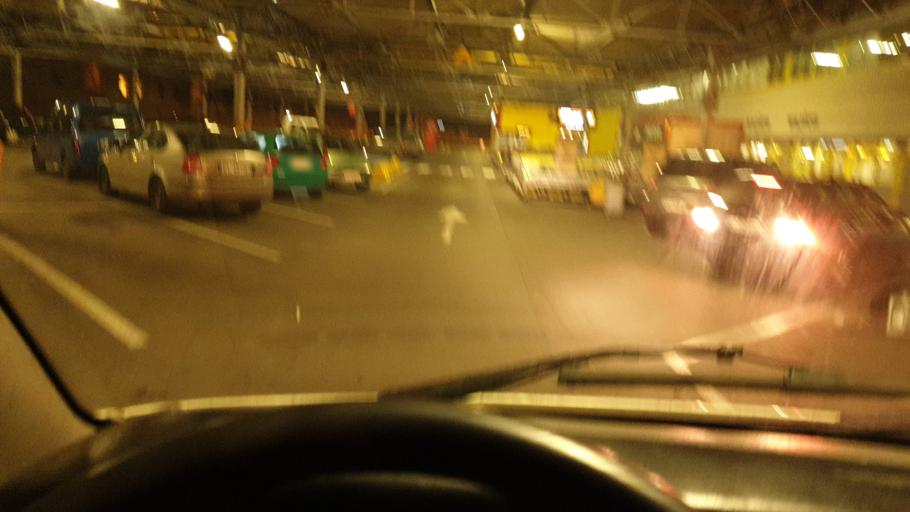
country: PL
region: Lodz Voivodeship
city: Lodz
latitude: 51.7188
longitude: 19.4401
